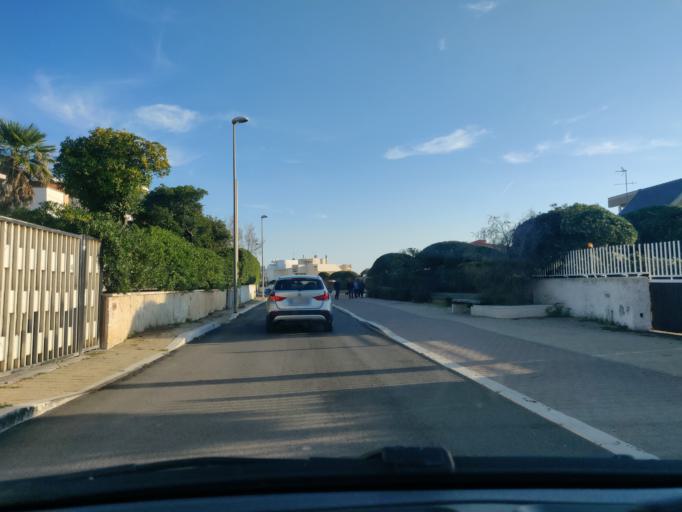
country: IT
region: Latium
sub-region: Citta metropolitana di Roma Capitale
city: Santa Marinella
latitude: 42.0309
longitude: 11.8348
